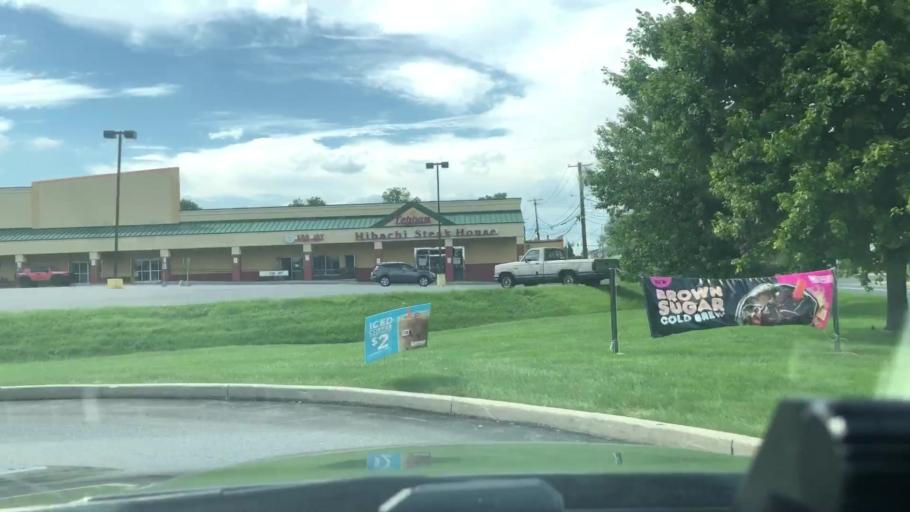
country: US
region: Pennsylvania
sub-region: Lehigh County
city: Dorneyville
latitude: 40.5799
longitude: -75.5233
